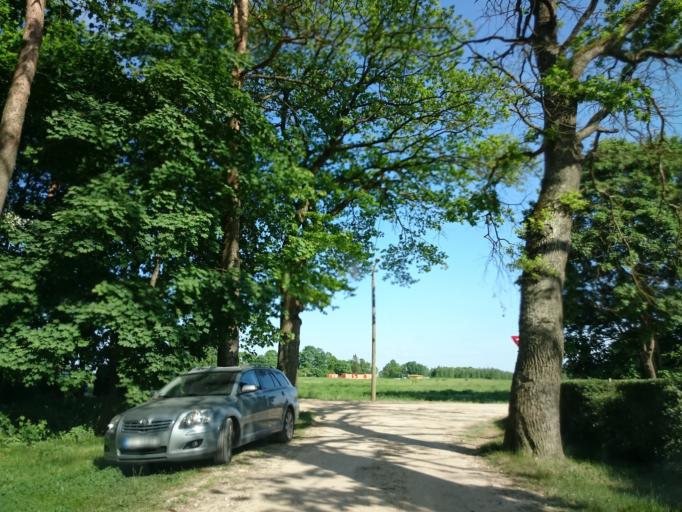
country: LV
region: Dobeles Rajons
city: Dobele
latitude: 56.6063
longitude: 23.2952
